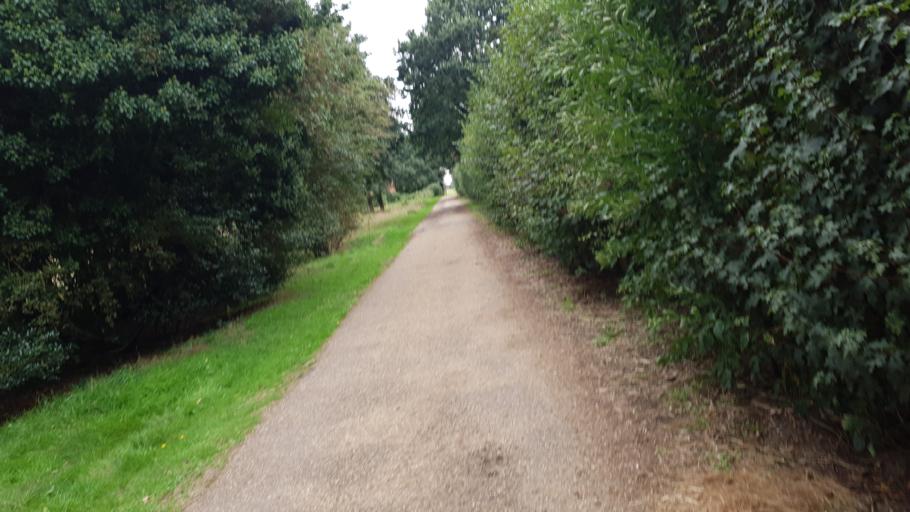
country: GB
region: England
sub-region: Essex
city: Manningtree
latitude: 51.9432
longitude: 1.0328
